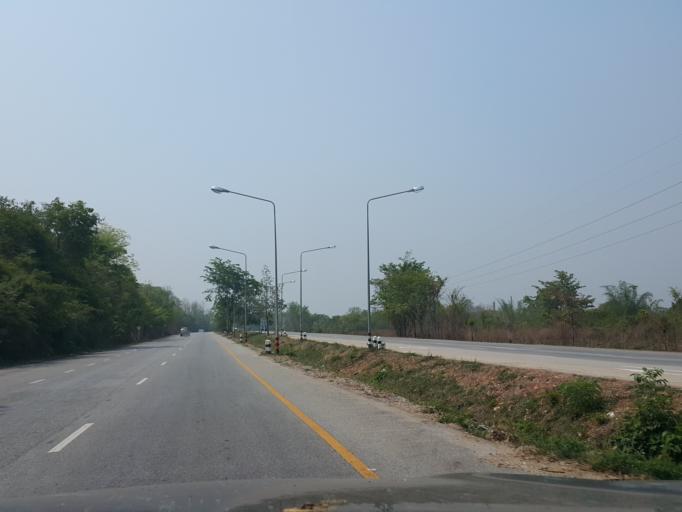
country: TH
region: Lampang
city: Thoen
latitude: 17.7021
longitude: 99.2319
